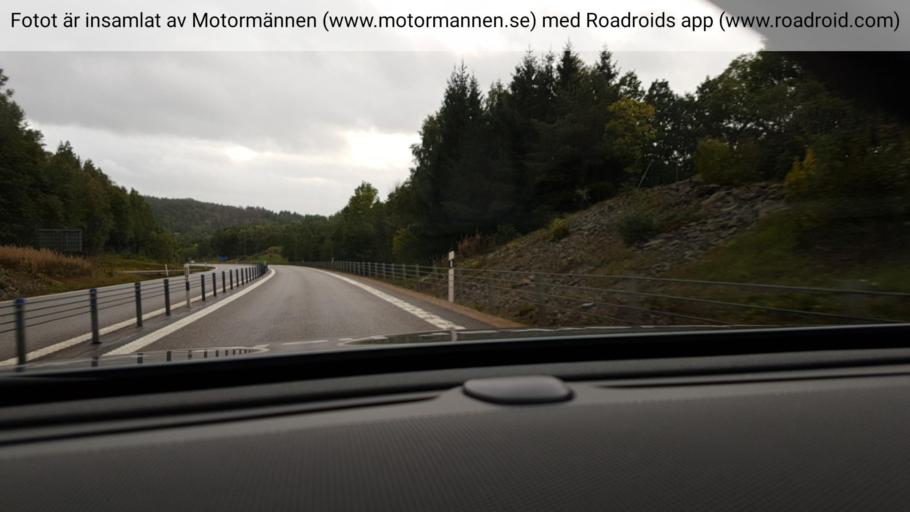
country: SE
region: Vaestra Goetaland
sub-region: Uddevalla Kommun
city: Uddevalla
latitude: 58.3211
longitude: 11.9476
